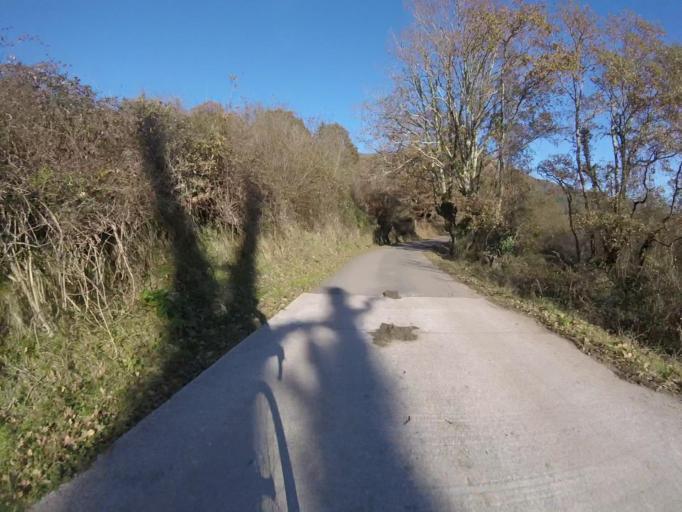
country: ES
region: Navarre
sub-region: Provincia de Navarra
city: Bera
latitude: 43.2967
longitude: -1.6588
